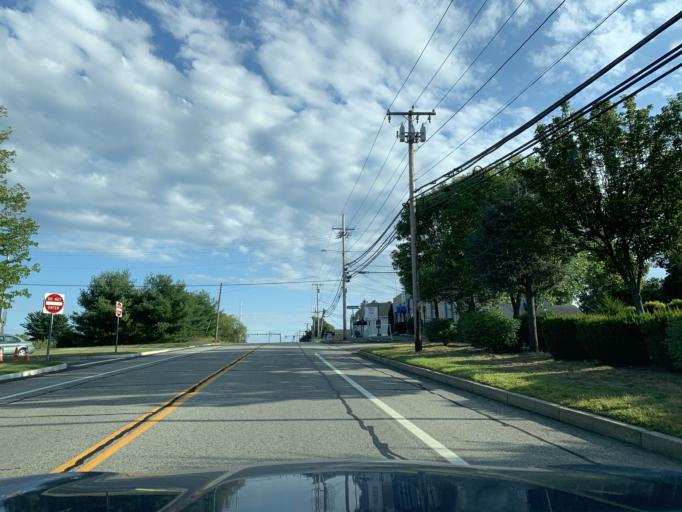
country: US
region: Rhode Island
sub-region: Kent County
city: West Warwick
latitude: 41.6905
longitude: -71.5012
